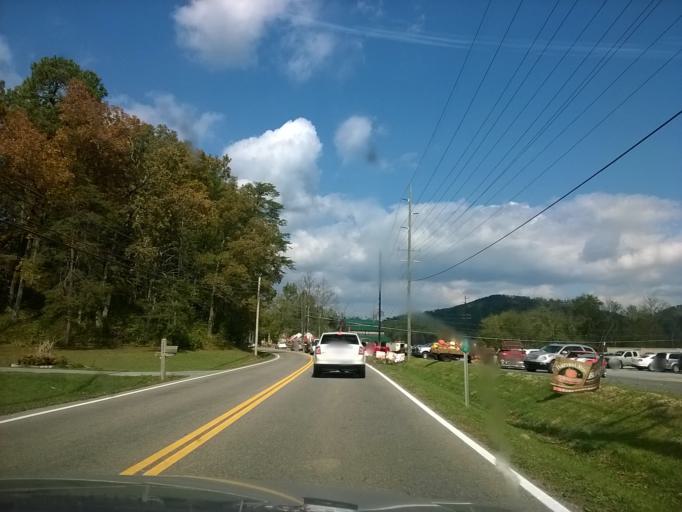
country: US
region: Tennessee
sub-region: Sevier County
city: Pigeon Forge
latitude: 35.7352
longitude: -83.6308
